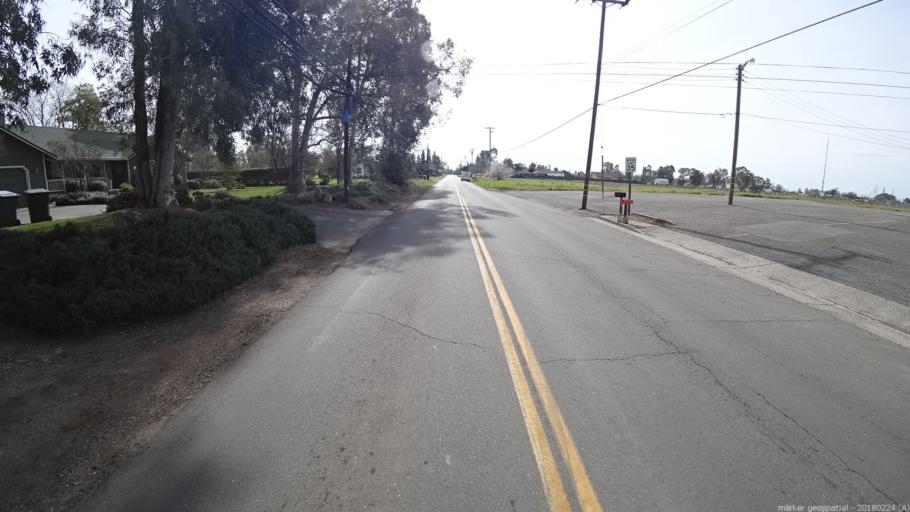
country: US
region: California
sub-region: Sacramento County
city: Elverta
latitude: 38.7142
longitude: -121.4666
